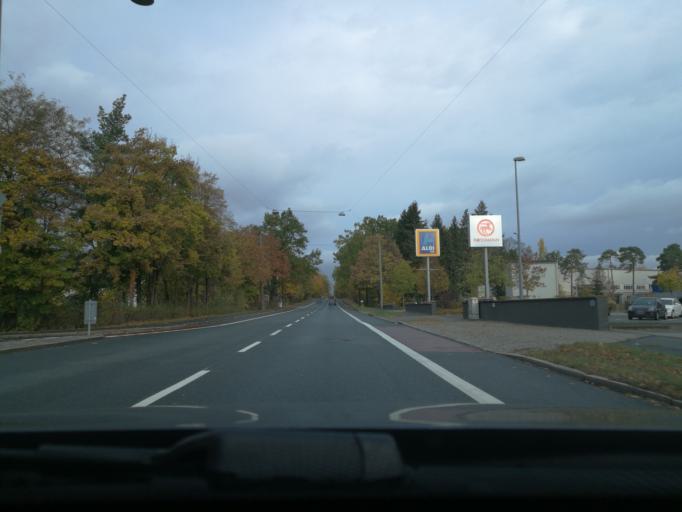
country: DE
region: Bavaria
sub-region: Regierungsbezirk Mittelfranken
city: Furth
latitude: 49.4936
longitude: 10.9889
